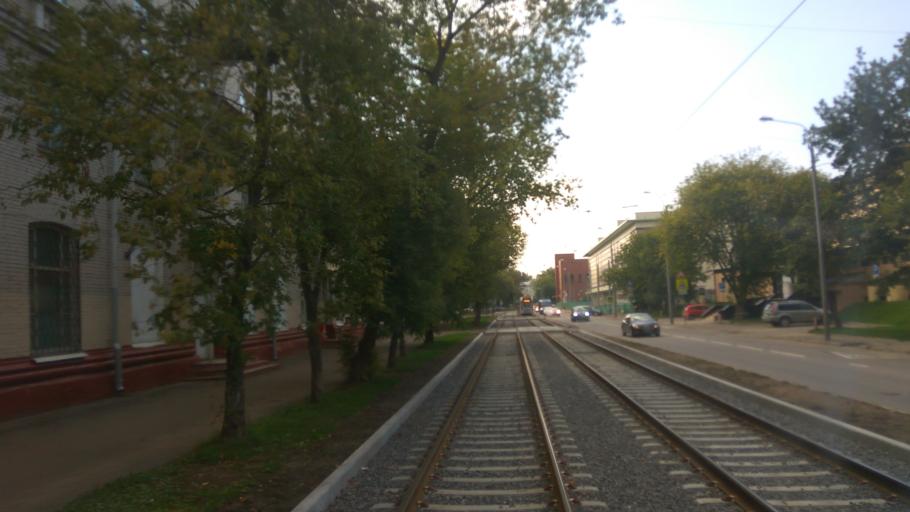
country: RU
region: Moskovskaya
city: Koptevo
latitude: 55.8241
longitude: 37.5170
